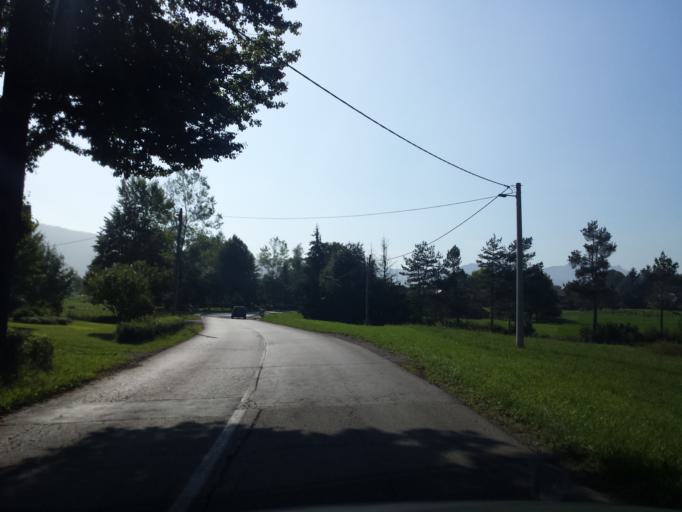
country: HR
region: Karlovacka
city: Ostarije
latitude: 45.2172
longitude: 15.2830
